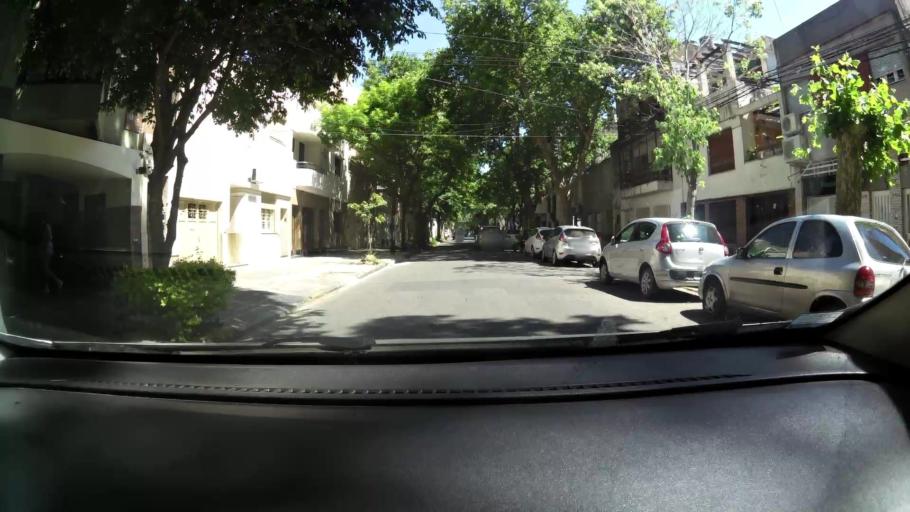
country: AR
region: Santa Fe
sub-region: Departamento de Rosario
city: Rosario
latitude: -32.9353
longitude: -60.6540
